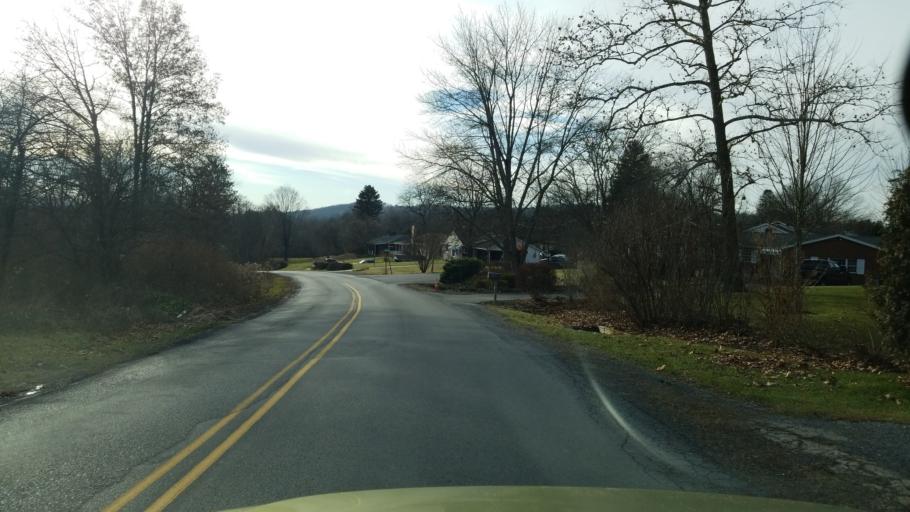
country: US
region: Pennsylvania
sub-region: Clearfield County
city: Clearfield
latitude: 41.0151
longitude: -78.4508
